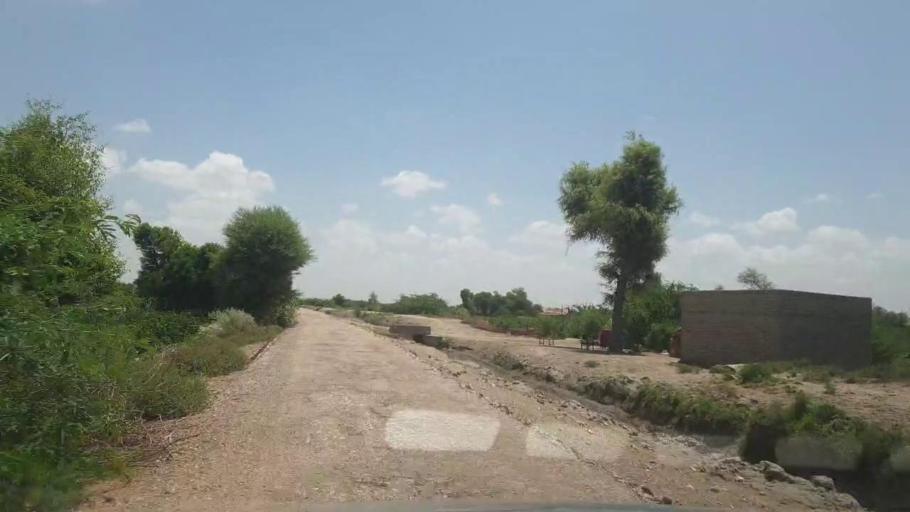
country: PK
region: Sindh
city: Kot Diji
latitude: 27.2909
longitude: 69.0880
